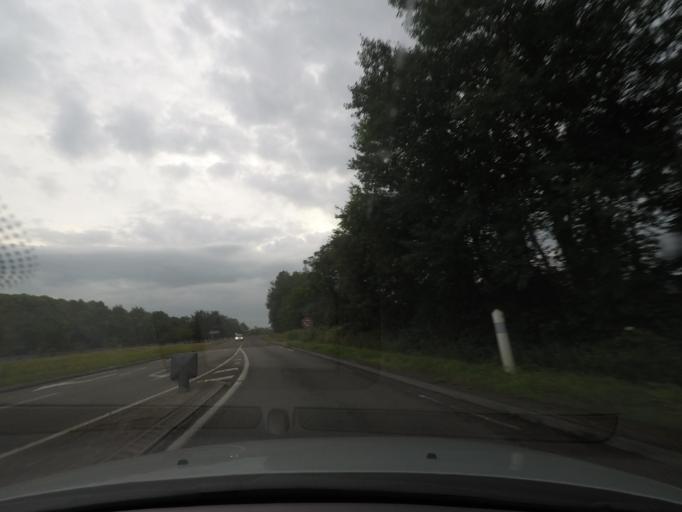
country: FR
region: Haute-Normandie
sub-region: Departement de la Seine-Maritime
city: Neufchatel-en-Bray
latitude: 49.7170
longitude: 1.4180
